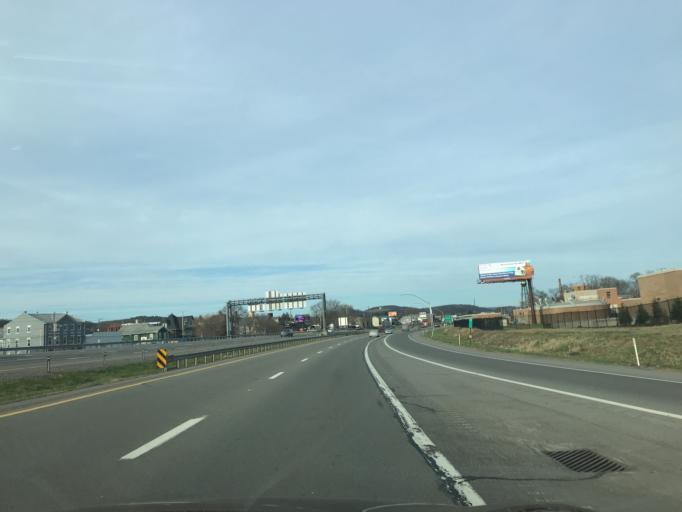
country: US
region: Pennsylvania
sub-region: Lycoming County
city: Williamsport
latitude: 41.2438
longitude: -76.9923
